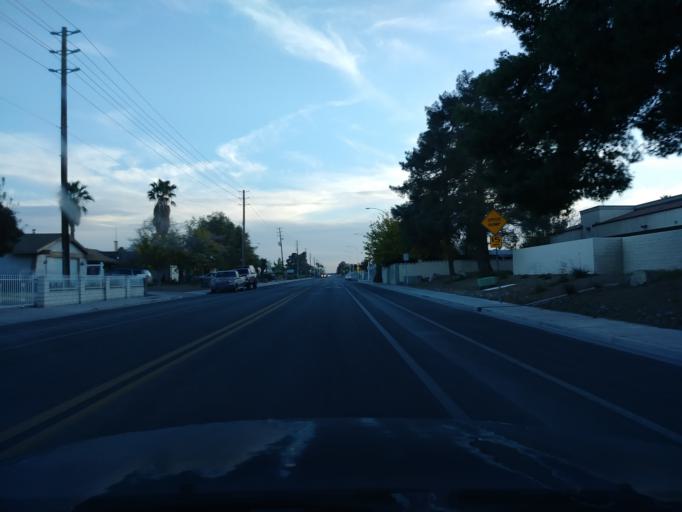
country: US
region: Nevada
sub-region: Clark County
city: Spring Valley
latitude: 36.1726
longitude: -115.2423
